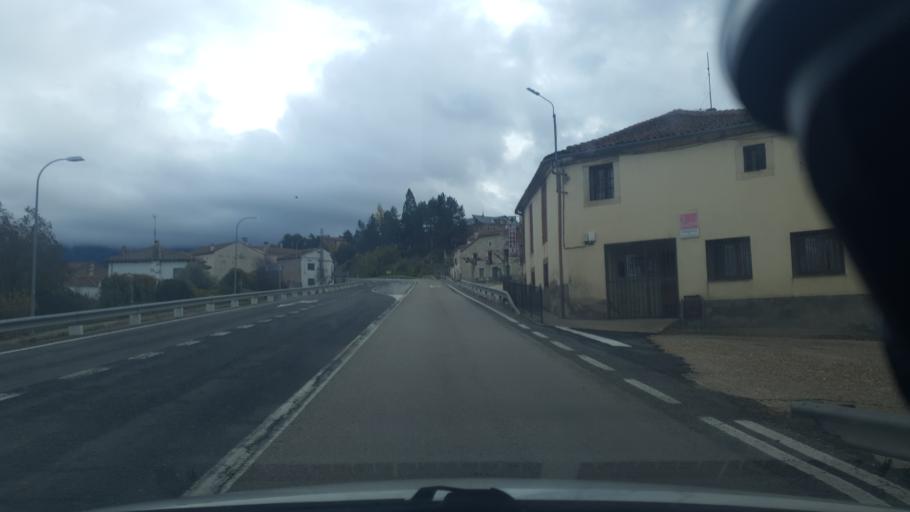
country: ES
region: Castille and Leon
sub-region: Provincia de Segovia
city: Cerezo de Abajo
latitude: 41.2185
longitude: -3.5908
